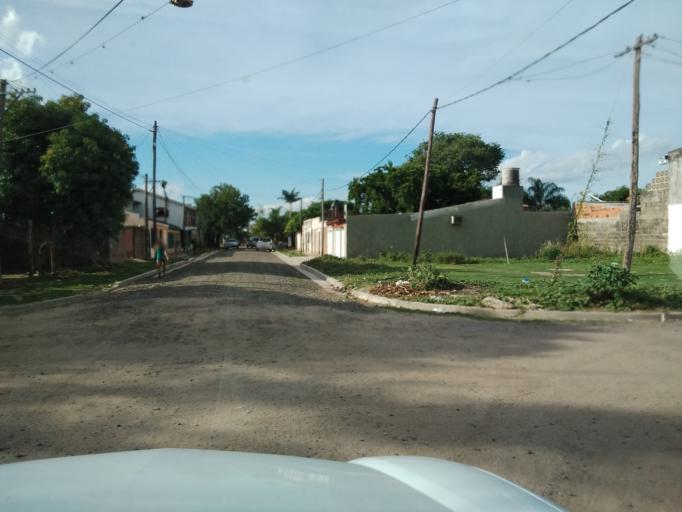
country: AR
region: Corrientes
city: Corrientes
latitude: -27.4920
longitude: -58.8431
